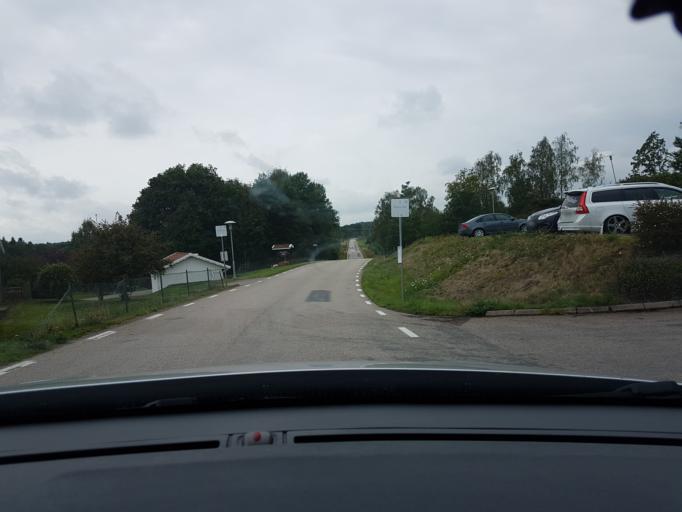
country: SE
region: Vaestra Goetaland
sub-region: Ale Kommun
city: Alvangen
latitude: 57.9118
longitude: 12.1545
